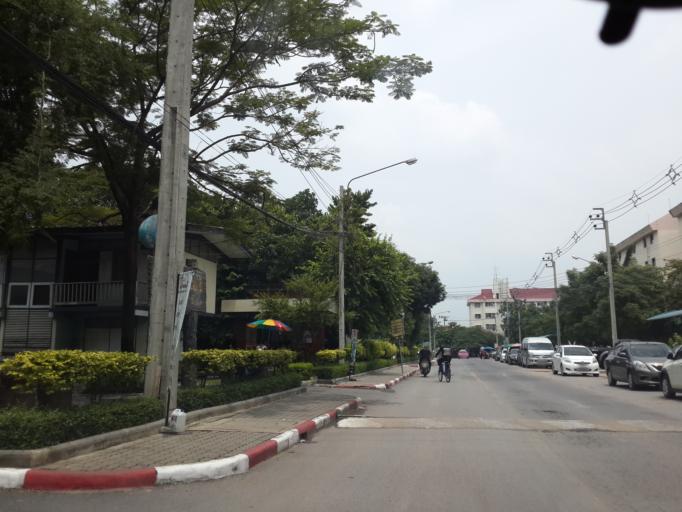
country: TH
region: Bangkok
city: Lak Si
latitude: 13.8742
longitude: 100.5900
